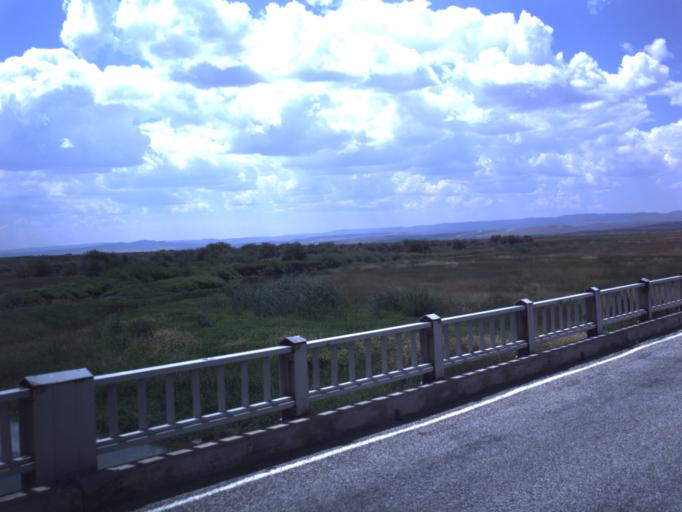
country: US
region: Utah
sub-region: Rich County
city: Randolph
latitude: 41.7771
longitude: -111.0735
